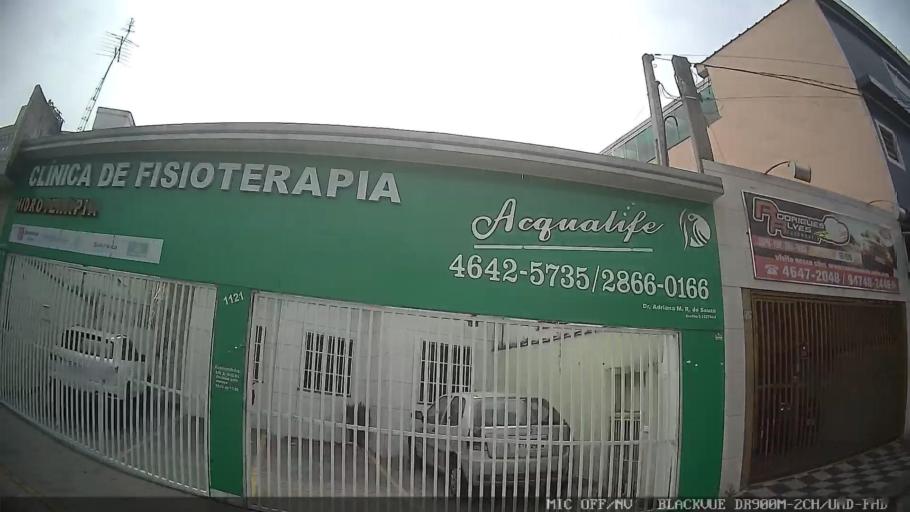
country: BR
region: Sao Paulo
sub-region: Itaquaquecetuba
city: Itaquaquecetuba
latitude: -23.4900
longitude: -46.3488
